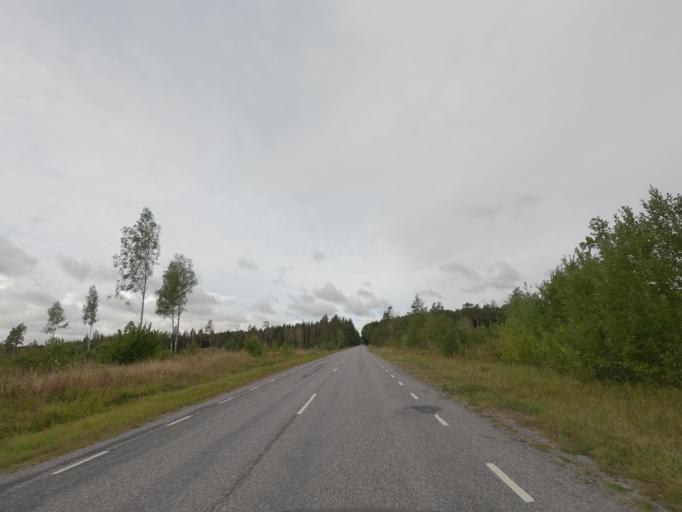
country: EE
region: Raplamaa
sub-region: Rapla vald
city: Rapla
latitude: 59.0064
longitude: 24.6185
